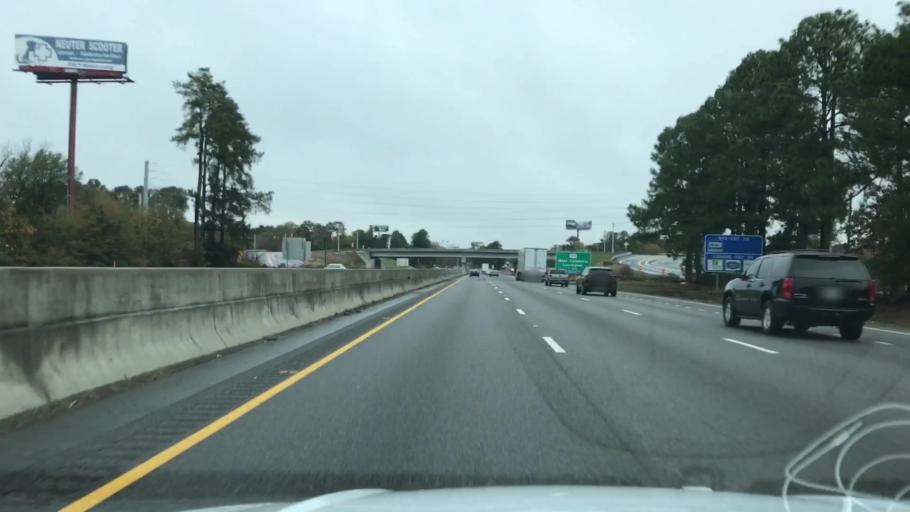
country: US
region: South Carolina
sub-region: Lexington County
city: Springdale
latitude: 33.9863
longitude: -81.1071
